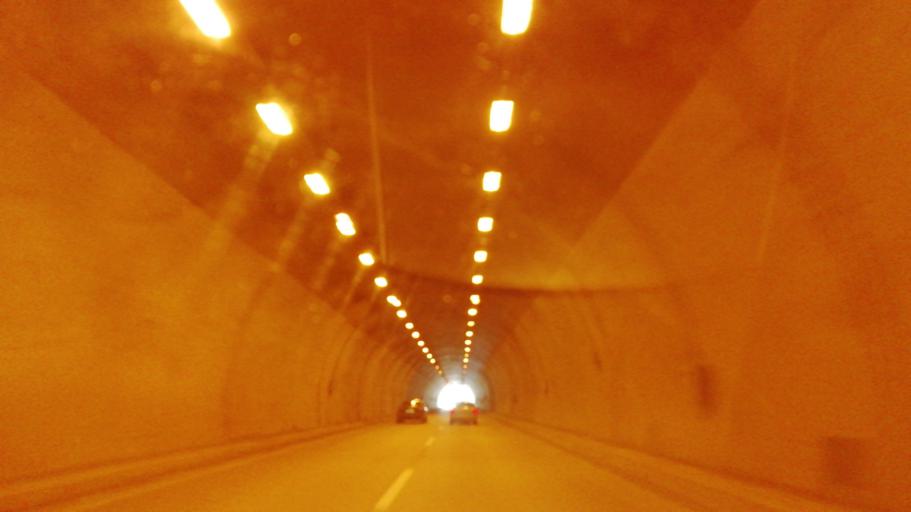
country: TR
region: Karabuk
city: Karabuk
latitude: 41.0813
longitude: 32.6713
